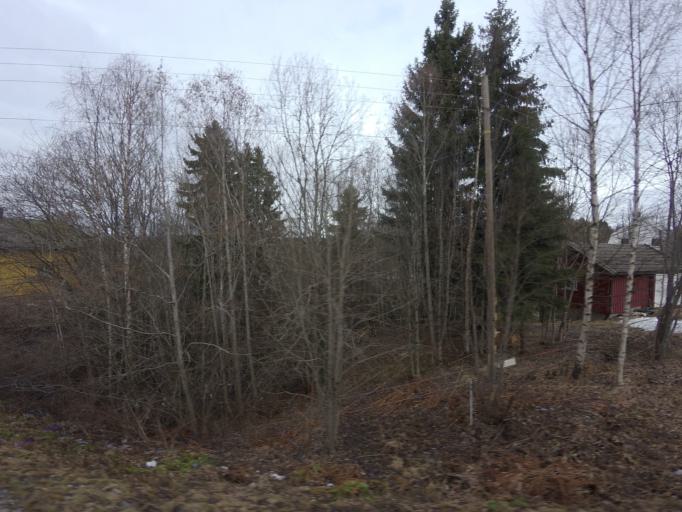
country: NO
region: Akershus
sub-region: Enebakk
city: Kirkebygda
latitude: 59.7758
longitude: 11.2760
